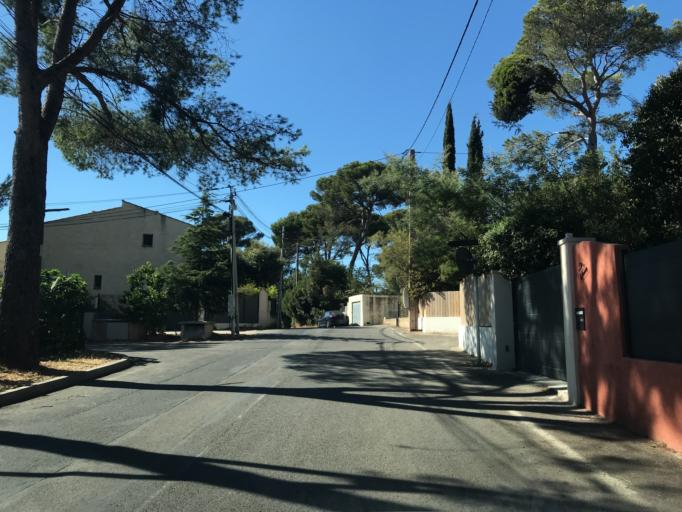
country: FR
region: Provence-Alpes-Cote d'Azur
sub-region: Departement du Var
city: La Seyne-sur-Mer
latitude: 43.0744
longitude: 5.8770
